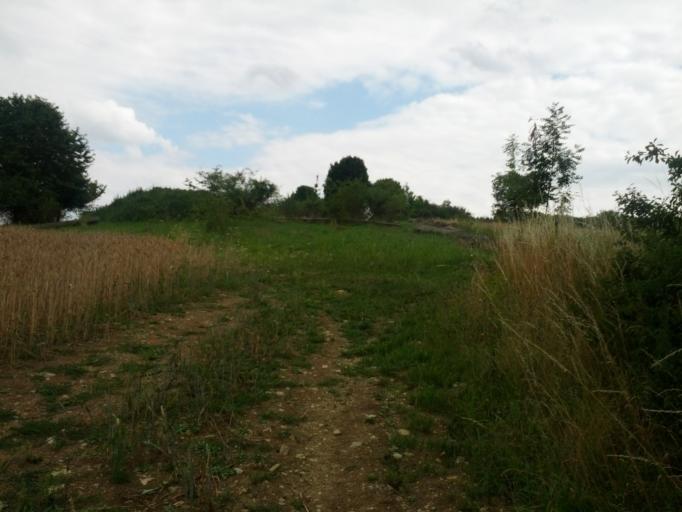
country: DE
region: Thuringia
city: Eisenach
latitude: 50.9970
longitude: 10.3243
